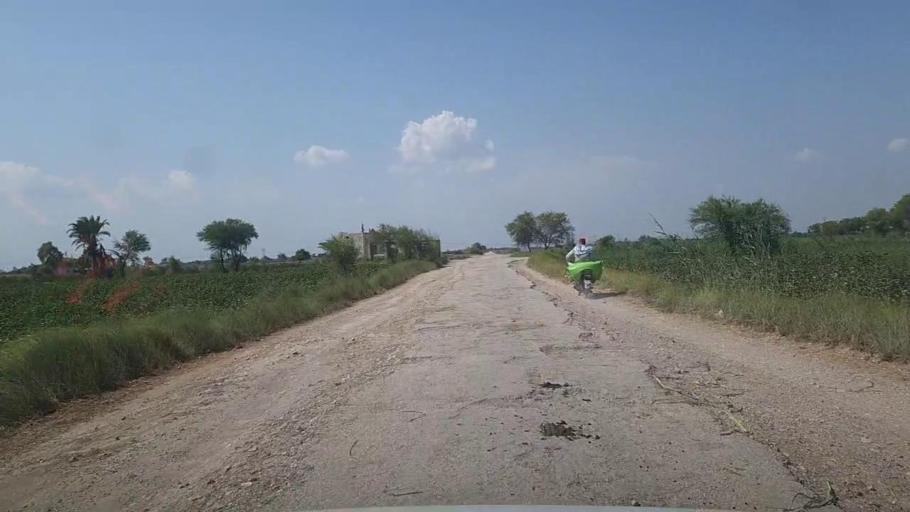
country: PK
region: Sindh
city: Khairpur
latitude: 28.0942
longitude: 69.6291
